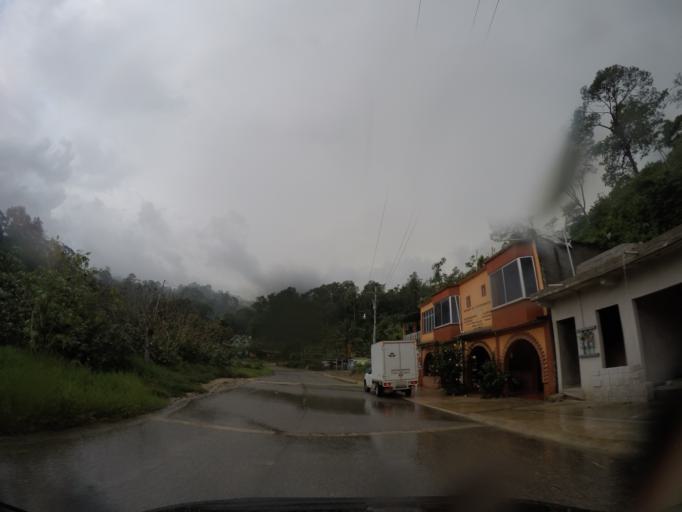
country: MX
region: Oaxaca
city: San Gabriel Mixtepec
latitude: 16.0881
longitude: -97.0801
